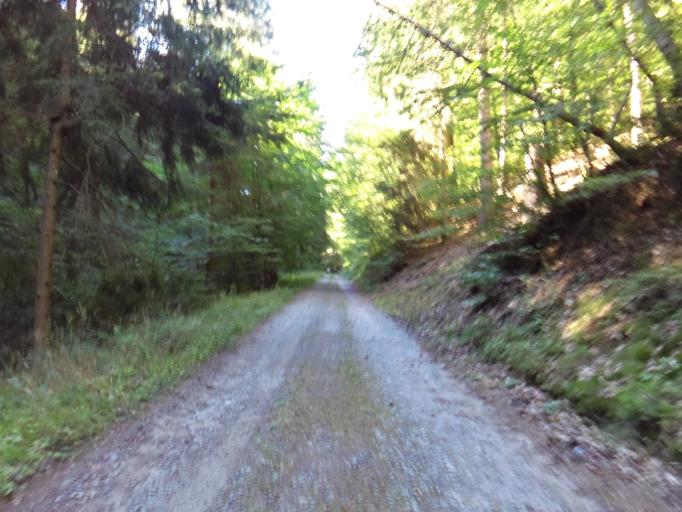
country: DE
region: Rheinland-Pfalz
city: Neidenfels
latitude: 49.4316
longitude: 8.0407
